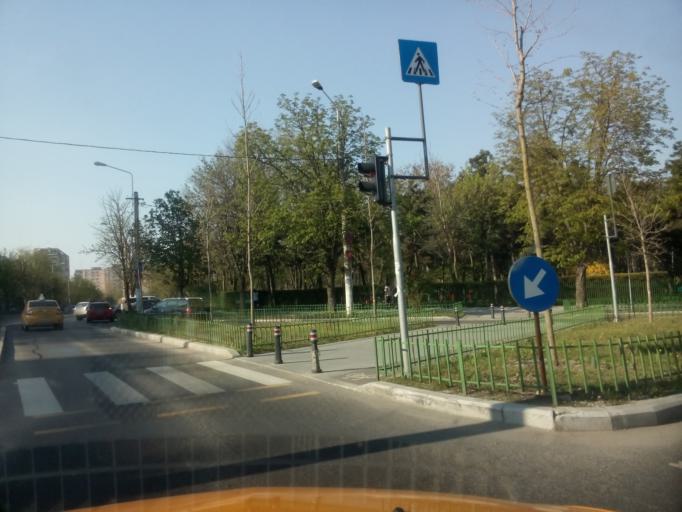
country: RO
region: Ilfov
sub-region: Comuna Fundeni-Dobroesti
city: Fundeni
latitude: 44.4234
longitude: 26.1508
